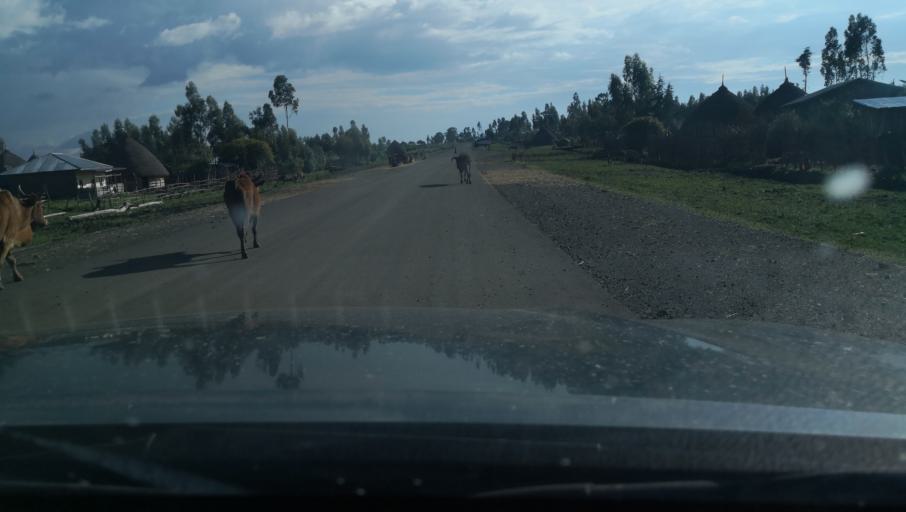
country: ET
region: Oromiya
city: Tulu Bolo
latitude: 8.4988
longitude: 38.2322
